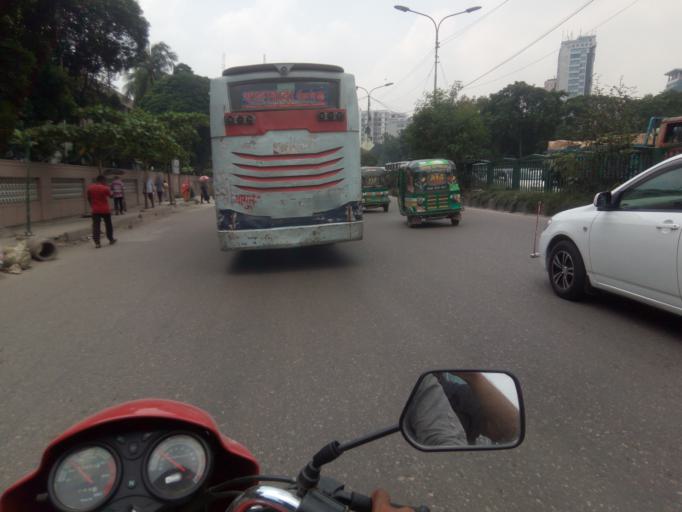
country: BD
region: Dhaka
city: Azimpur
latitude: 23.7494
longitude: 90.3936
